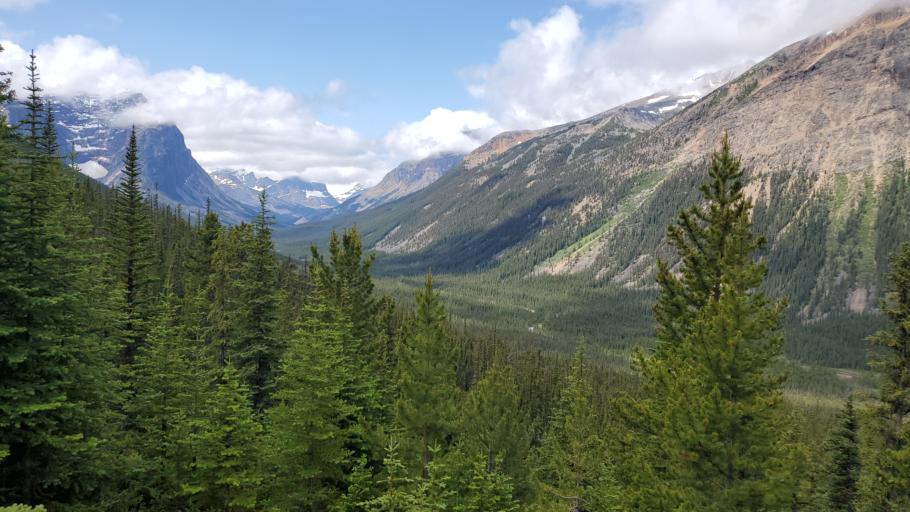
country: CA
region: Alberta
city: Jasper Park Lodge
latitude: 52.7044
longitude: -118.0606
